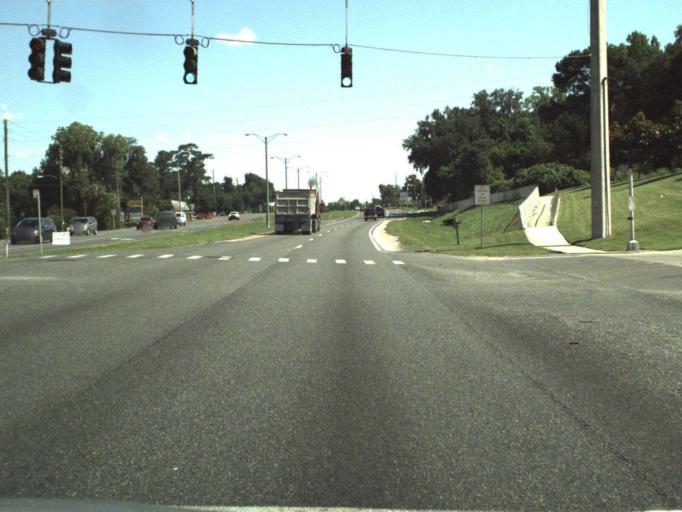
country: US
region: Florida
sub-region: Marion County
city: Belleview
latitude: 29.0713
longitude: -82.0716
